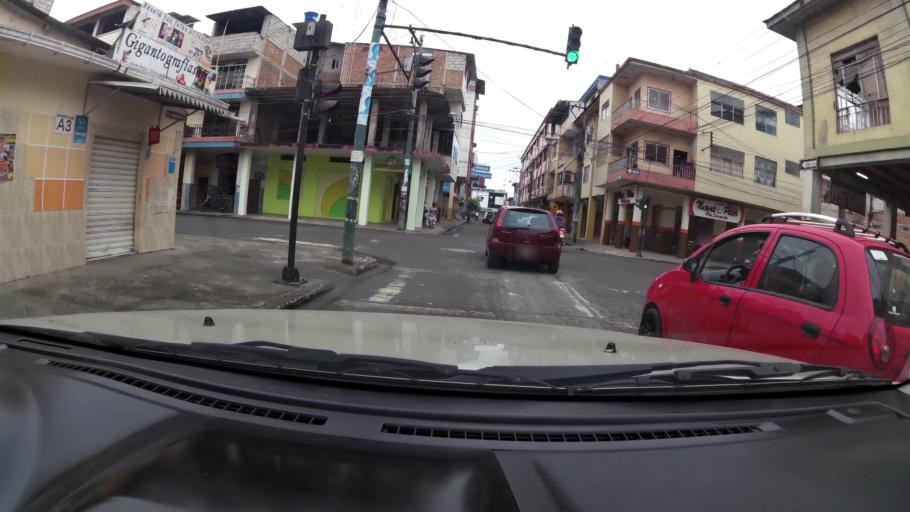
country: EC
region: El Oro
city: Pasaje
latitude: -3.3283
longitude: -79.8065
